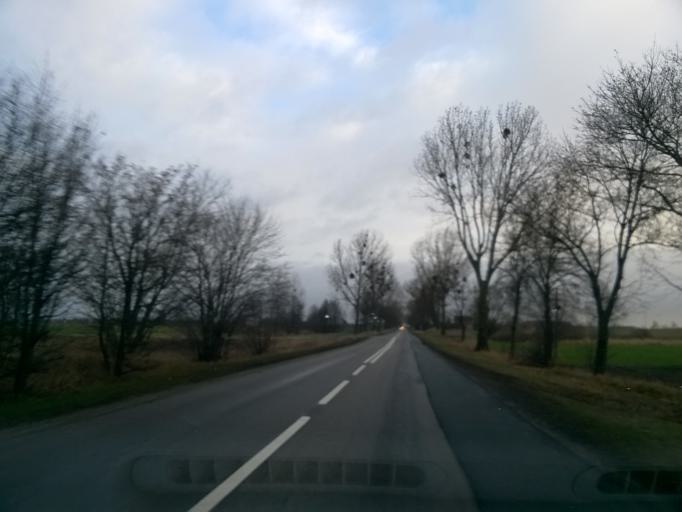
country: PL
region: Greater Poland Voivodeship
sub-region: Powiat wagrowiecki
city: Golancz
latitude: 52.8604
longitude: 17.2807
